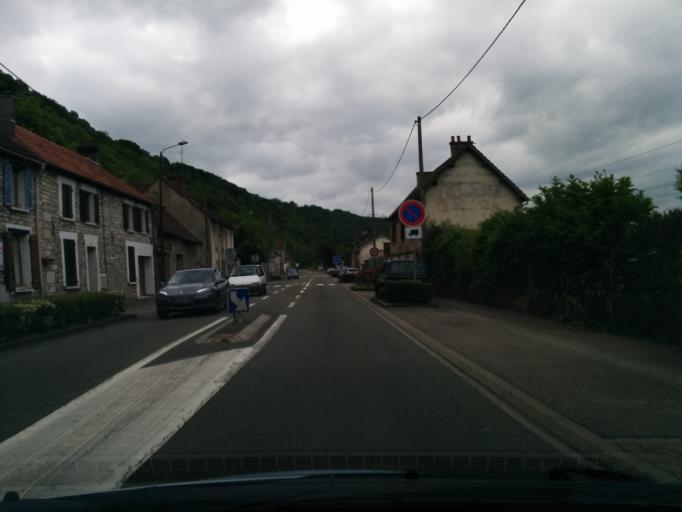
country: FR
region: Ile-de-France
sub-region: Departement des Yvelines
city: Bennecourt
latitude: 49.0351
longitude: 1.5467
